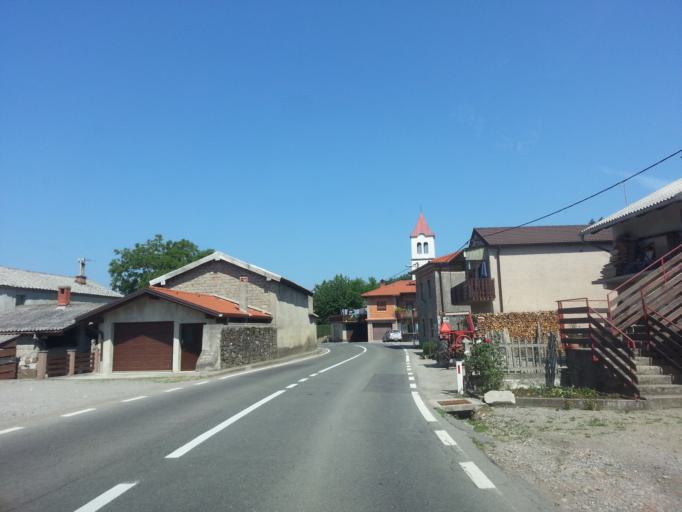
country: SI
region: Ilirska Bistrica
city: Ilirska Bistrica
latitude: 45.5056
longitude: 14.2674
